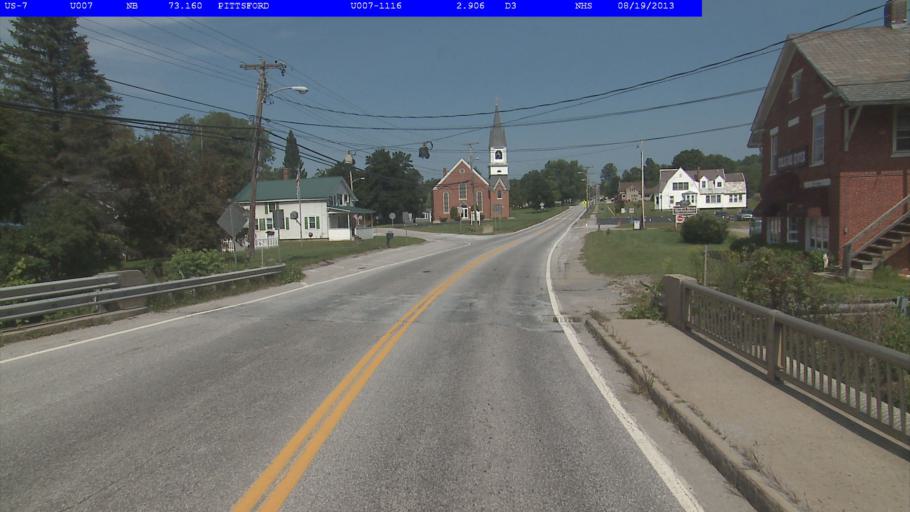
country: US
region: Vermont
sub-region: Rutland County
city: Rutland
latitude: 43.7012
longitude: -73.0112
